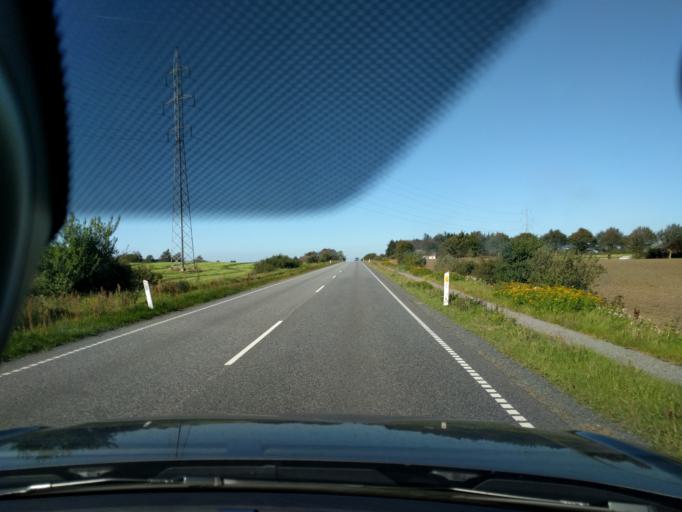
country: DK
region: North Denmark
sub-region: Vesthimmerland Kommune
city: Alestrup
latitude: 56.7267
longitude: 9.6068
